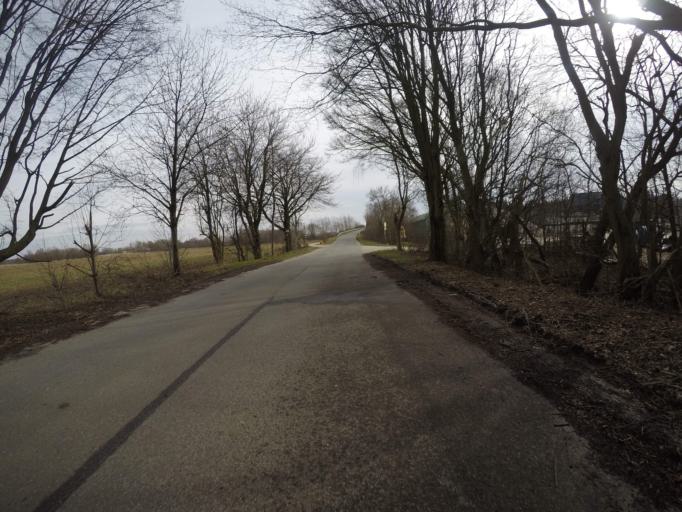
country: DE
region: North Rhine-Westphalia
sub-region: Regierungsbezirk Munster
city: Isselburg
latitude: 51.8149
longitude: 6.5166
